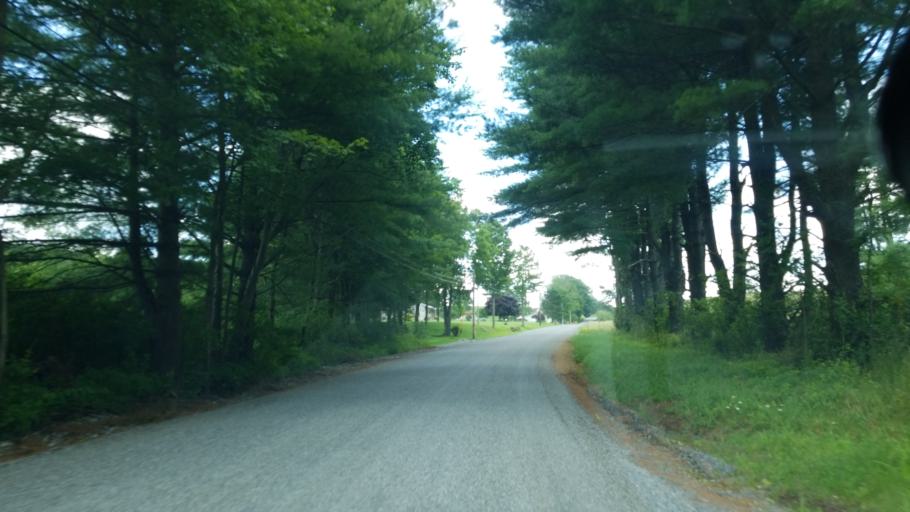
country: US
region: Pennsylvania
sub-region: Jefferson County
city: Brookville
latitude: 41.2321
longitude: -79.0080
